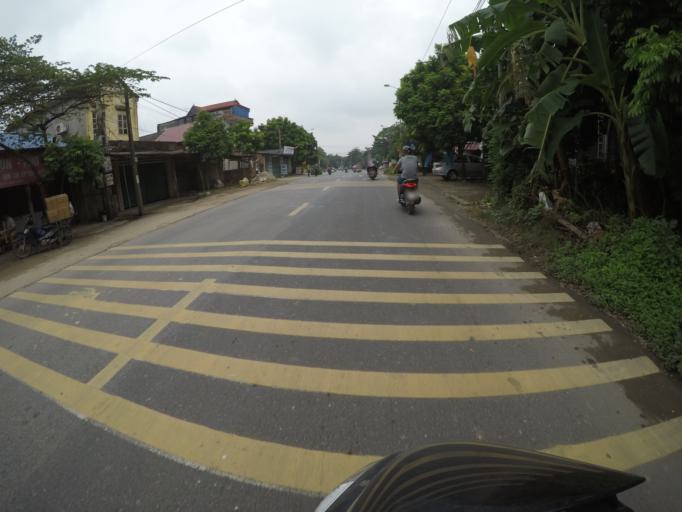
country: VN
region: Ha Noi
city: Soc Son
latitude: 21.2691
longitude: 105.8548
